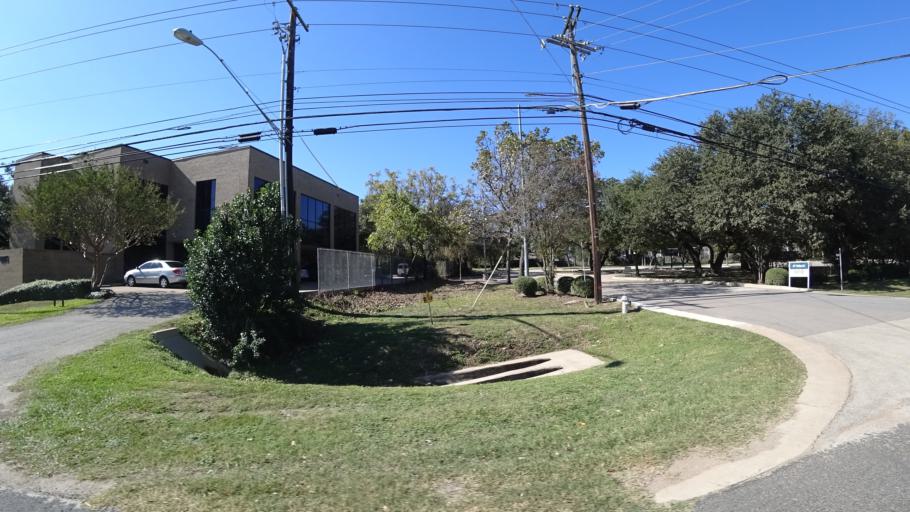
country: US
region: Texas
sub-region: Williamson County
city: Jollyville
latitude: 30.3852
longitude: -97.7454
